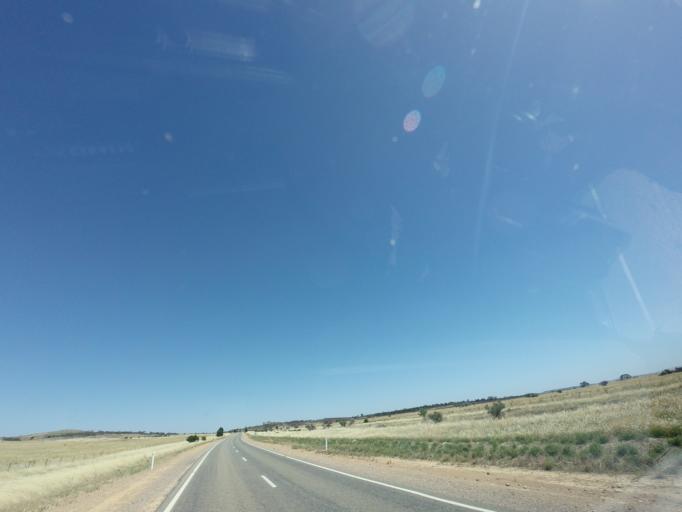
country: AU
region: South Australia
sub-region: Peterborough
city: Peterborough
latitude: -32.8985
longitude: 138.7561
